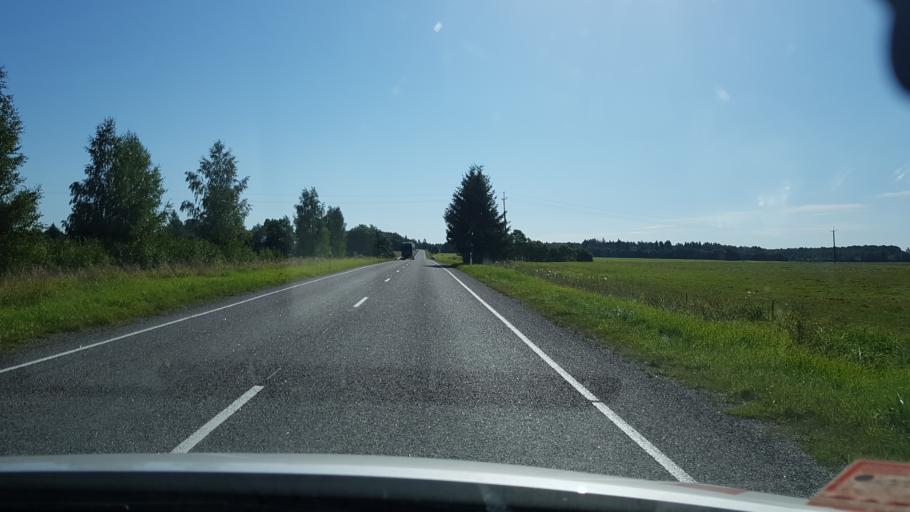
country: EE
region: Tartu
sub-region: Tartu linn
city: Tartu
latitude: 58.4678
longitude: 26.7321
